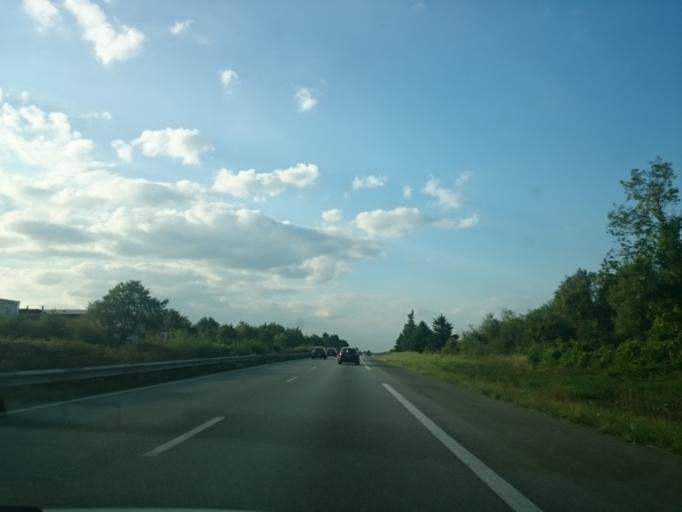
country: FR
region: Pays de la Loire
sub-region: Departement de la Loire-Atlantique
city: Sautron
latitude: 47.2469
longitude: -1.6747
